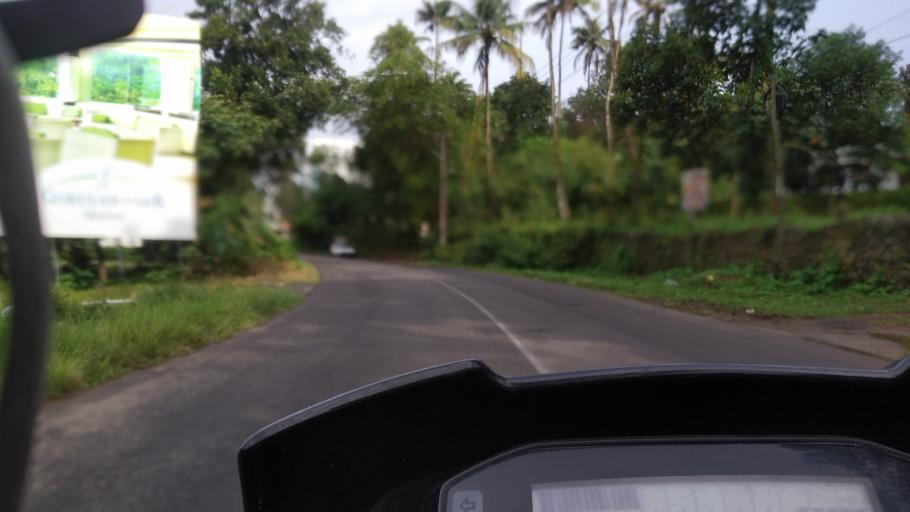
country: IN
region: Kerala
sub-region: Ernakulam
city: Kotamangalam
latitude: 10.0496
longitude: 76.7201
